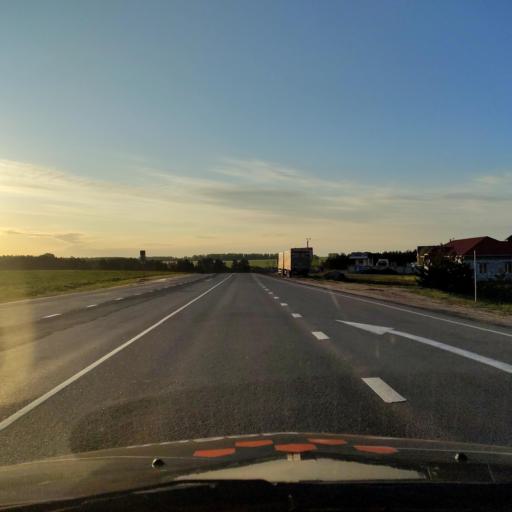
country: RU
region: Orjol
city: Livny
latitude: 52.4495
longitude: 37.5068
